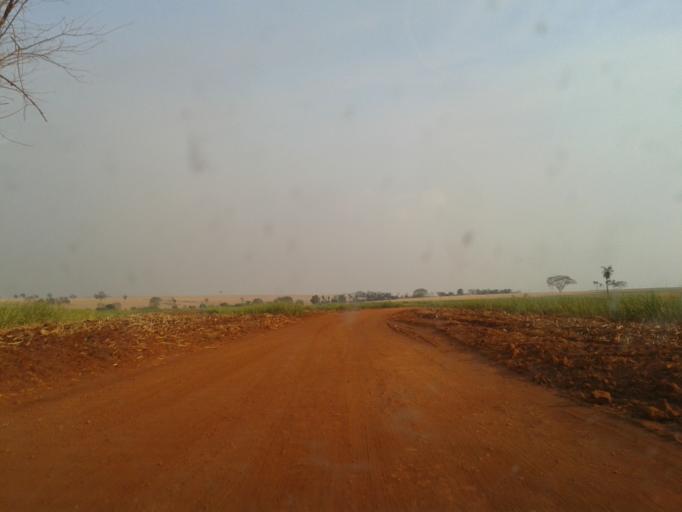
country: BR
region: Minas Gerais
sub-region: Capinopolis
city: Capinopolis
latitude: -18.7237
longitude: -49.6840
